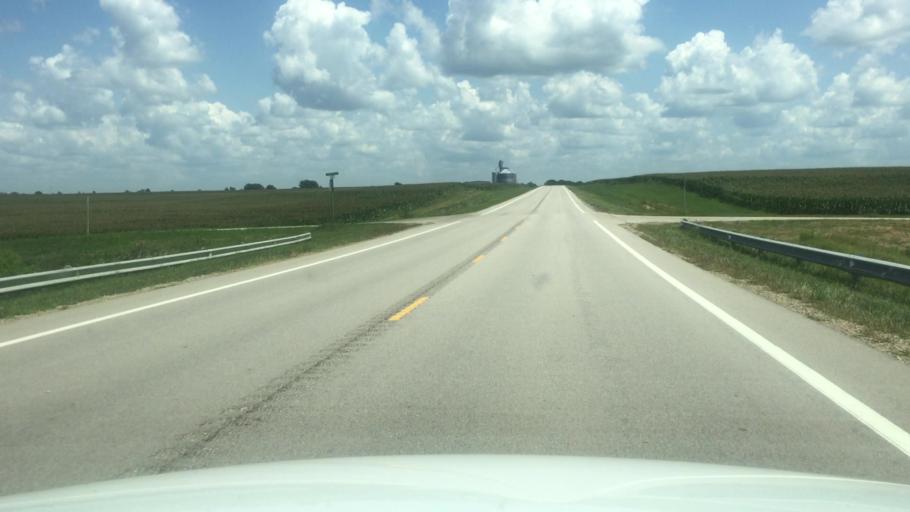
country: US
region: Kansas
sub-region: Brown County
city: Horton
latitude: 39.6601
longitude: -95.3963
